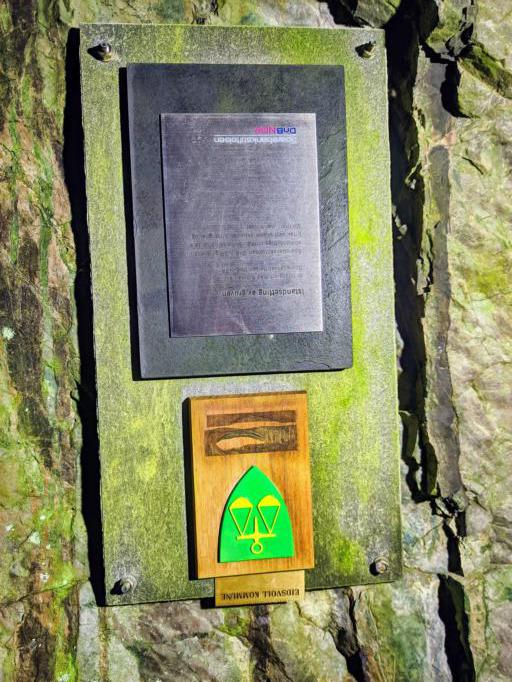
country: NO
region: Akershus
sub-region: Hurdal
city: Hurdal
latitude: 60.5587
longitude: 11.1403
